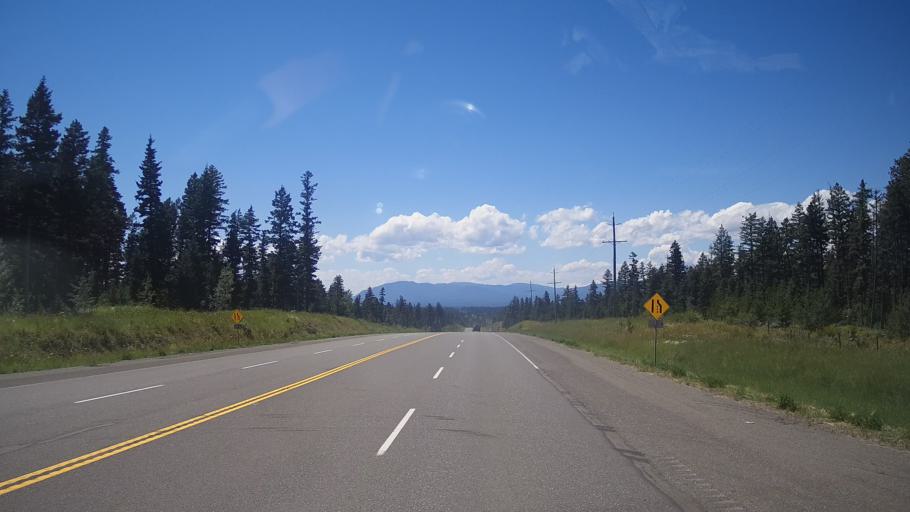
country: CA
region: British Columbia
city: Cache Creek
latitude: 51.2694
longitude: -121.4497
